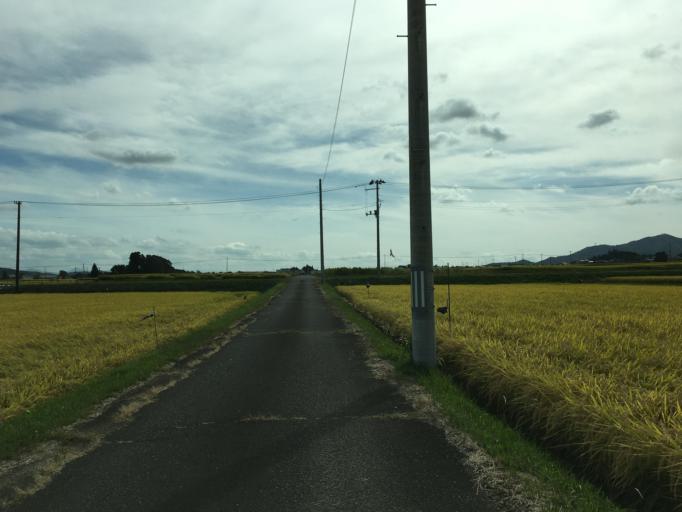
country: JP
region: Fukushima
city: Motomiya
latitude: 37.5571
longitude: 140.3859
